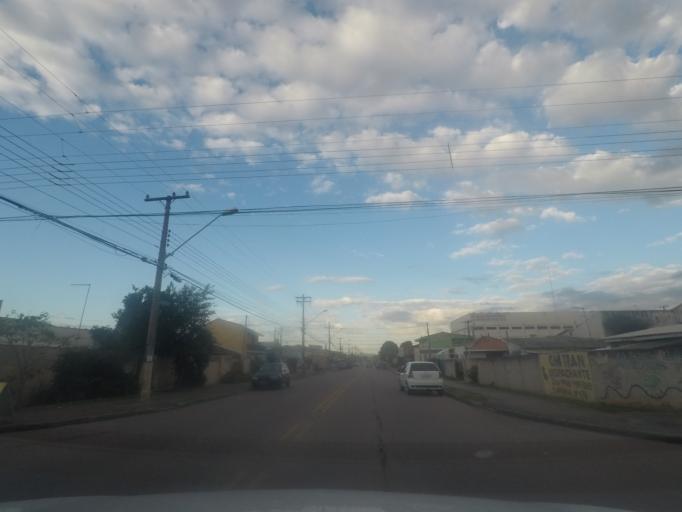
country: BR
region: Parana
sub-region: Pinhais
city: Pinhais
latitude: -25.4665
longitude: -49.2028
